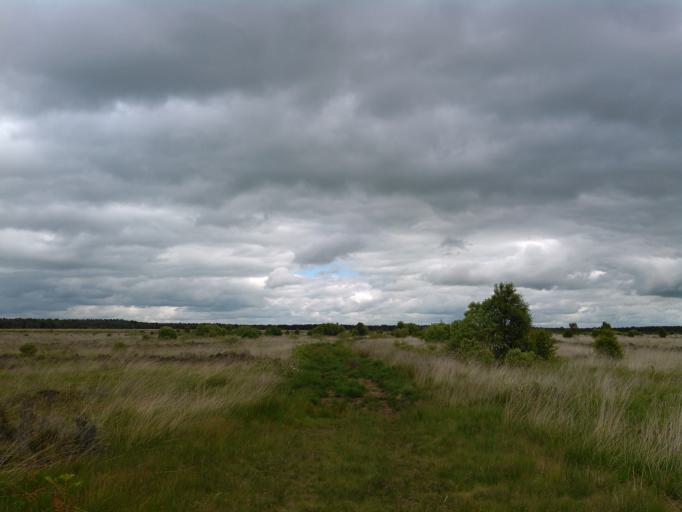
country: GB
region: England
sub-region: Shropshire
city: Wem
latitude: 52.9266
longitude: -2.7567
